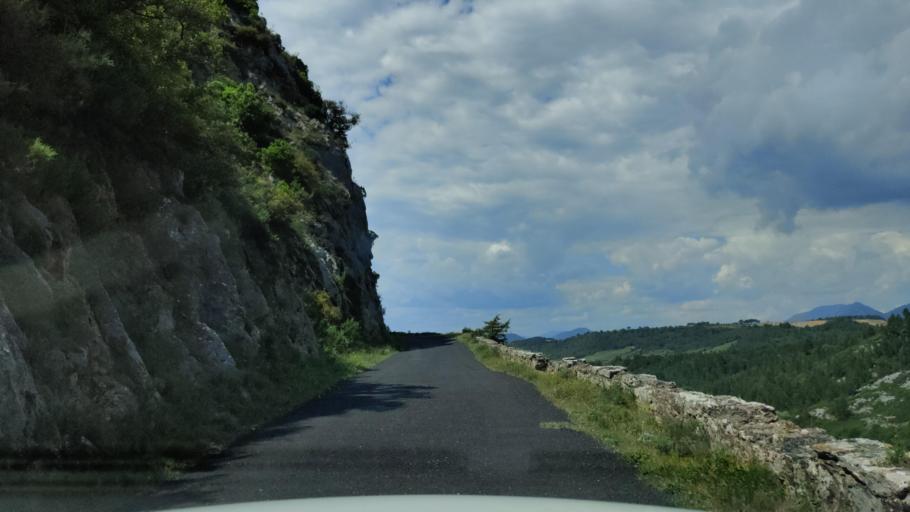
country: FR
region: Languedoc-Roussillon
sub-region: Departement des Pyrenees-Orientales
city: Estagel
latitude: 42.8012
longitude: 2.7298
